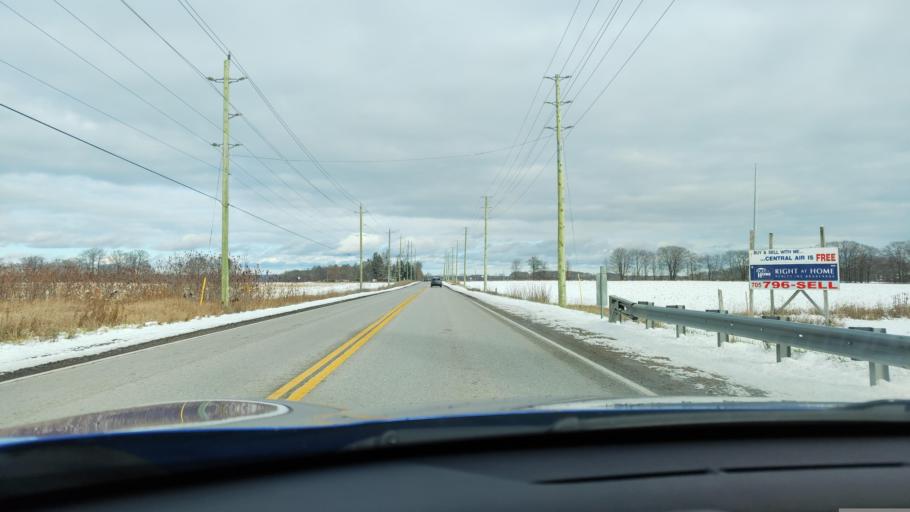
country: CA
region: Ontario
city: Barrie
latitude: 44.3956
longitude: -79.7477
